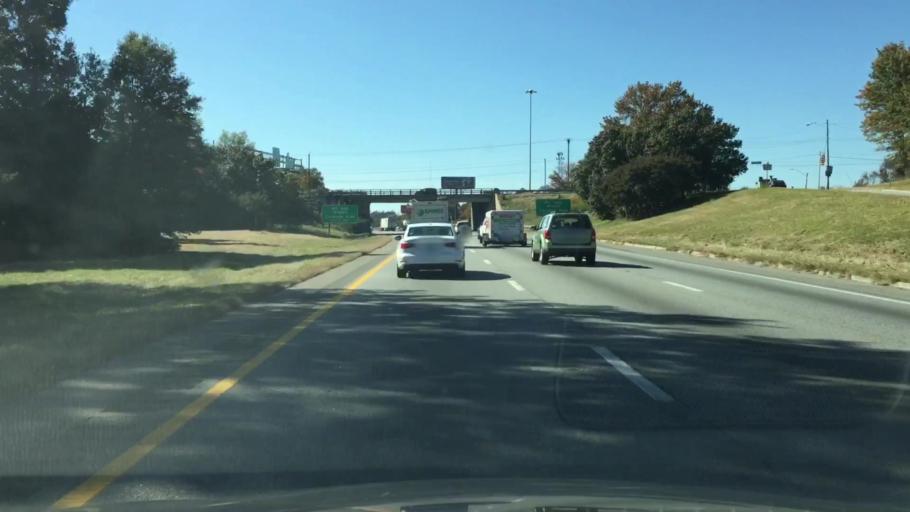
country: US
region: North Carolina
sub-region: Guilford County
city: Greensboro
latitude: 36.0343
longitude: -79.7989
